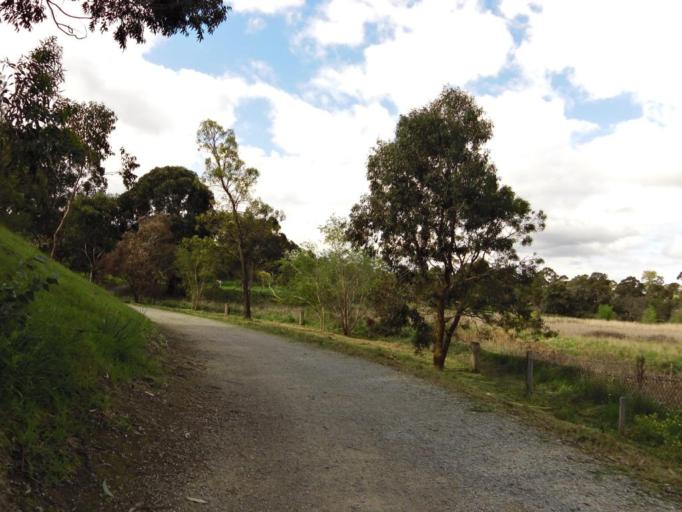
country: AU
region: Victoria
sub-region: Banyule
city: Viewbank
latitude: -37.7458
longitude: 145.0862
